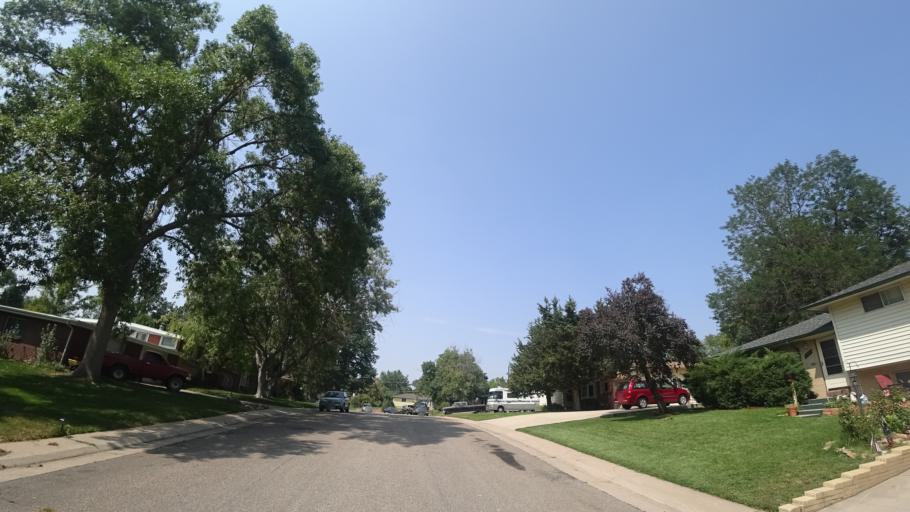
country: US
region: Colorado
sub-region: Arapahoe County
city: Littleton
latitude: 39.6265
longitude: -104.9999
